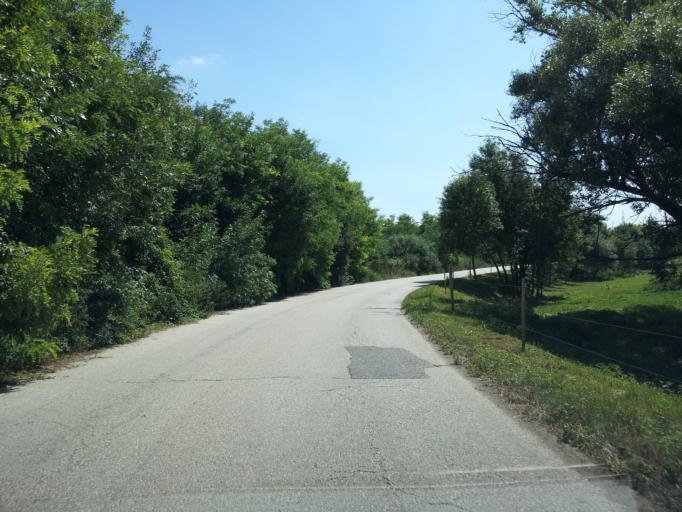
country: HU
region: Fejer
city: Many
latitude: 47.5309
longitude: 18.5854
